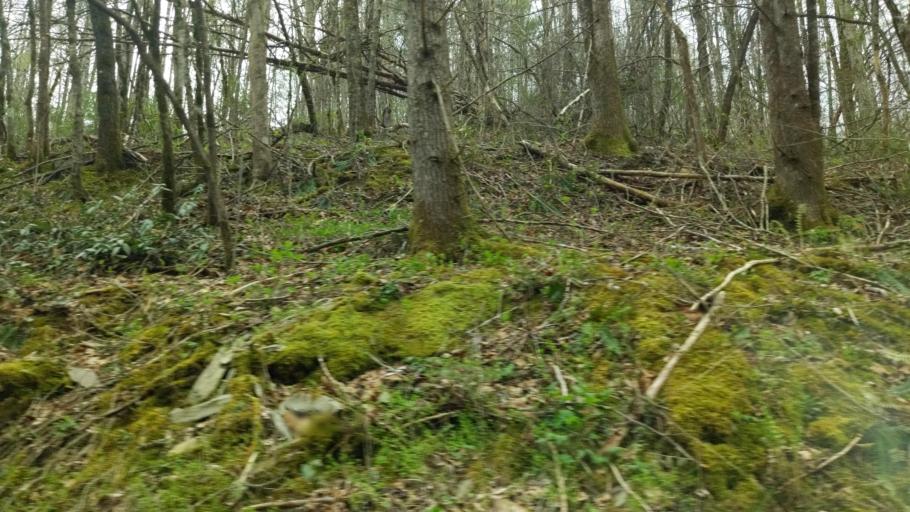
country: US
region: Tennessee
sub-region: Sevier County
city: Gatlinburg
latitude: 35.7211
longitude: -83.4822
